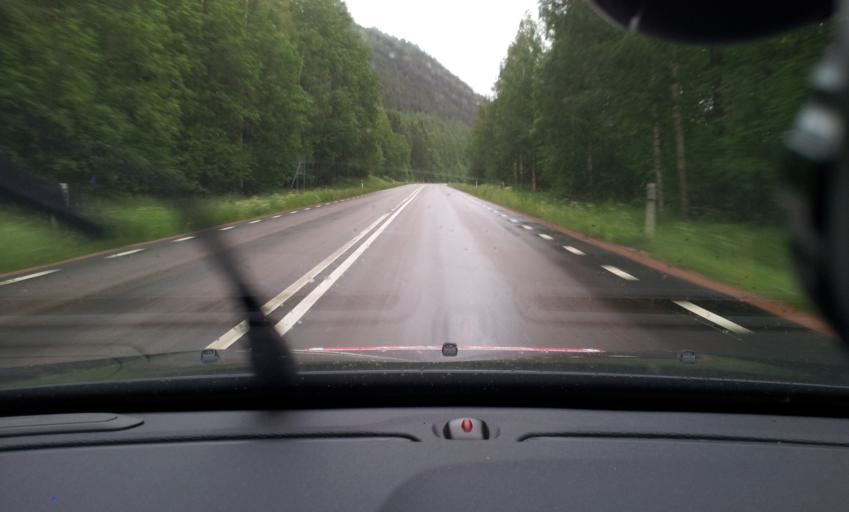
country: SE
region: Jaemtland
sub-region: Ragunda Kommun
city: Hammarstrand
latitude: 63.1402
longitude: 16.0131
